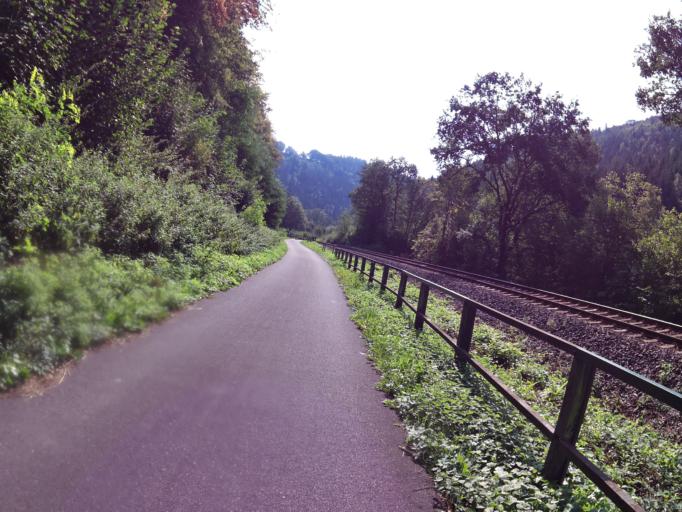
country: DE
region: Rheinland-Pfalz
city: Dahlem
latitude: 49.9124
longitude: 6.6119
